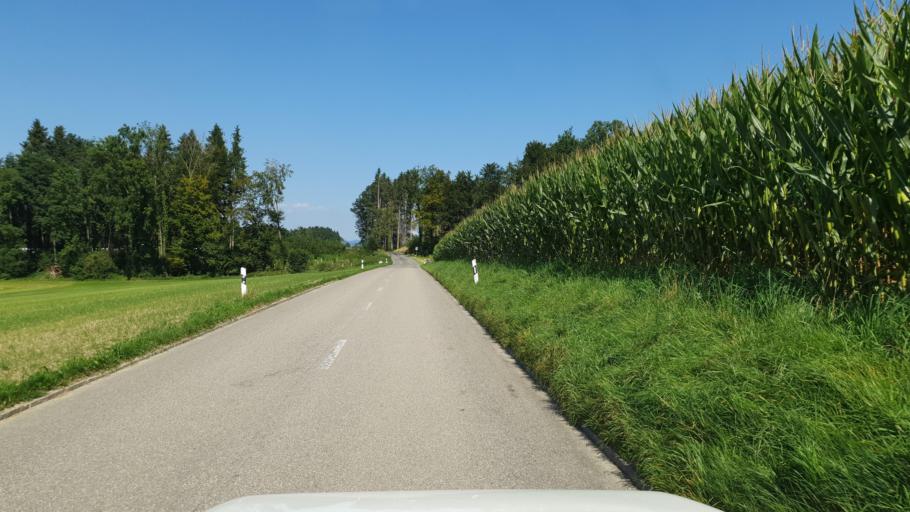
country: CH
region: Lucerne
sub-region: Hochdorf District
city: Inwil
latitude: 47.1516
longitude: 8.3601
